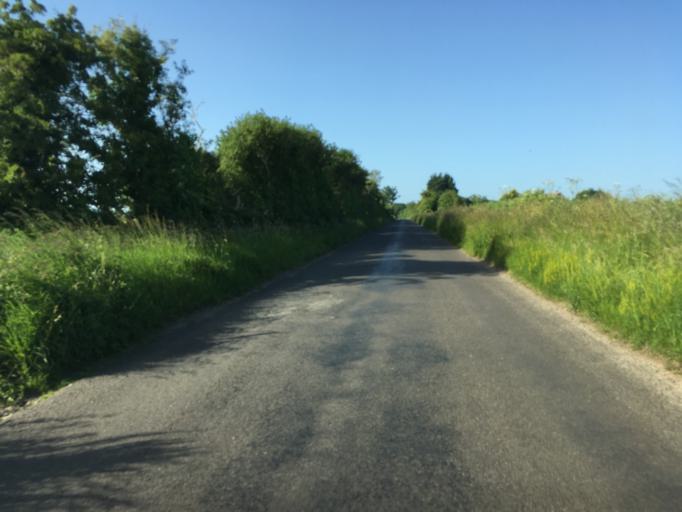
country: GB
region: England
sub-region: Oxfordshire
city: Burford
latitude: 51.8286
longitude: -1.6370
